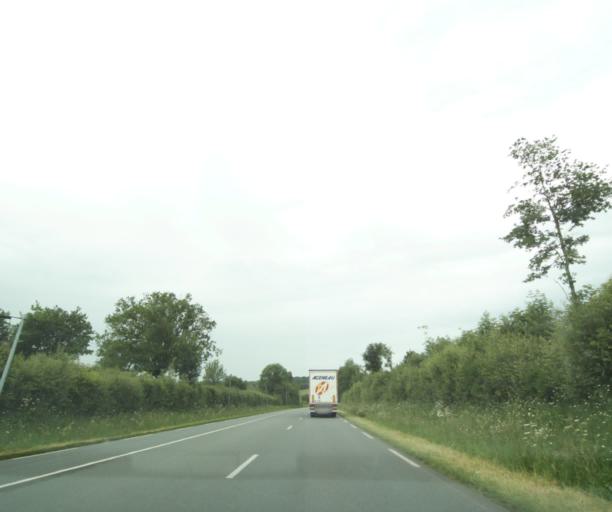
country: FR
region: Poitou-Charentes
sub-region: Departement des Deux-Sevres
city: Saint-Pardoux
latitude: 46.5850
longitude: -0.2925
